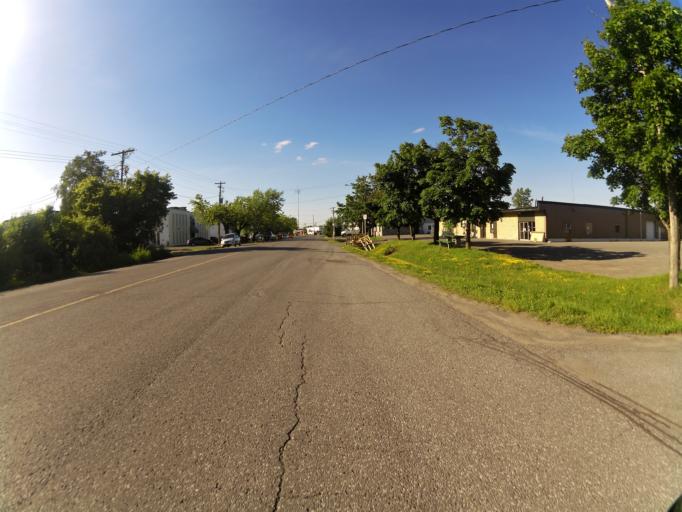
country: CA
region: Ontario
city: Ottawa
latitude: 45.3229
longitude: -75.7214
